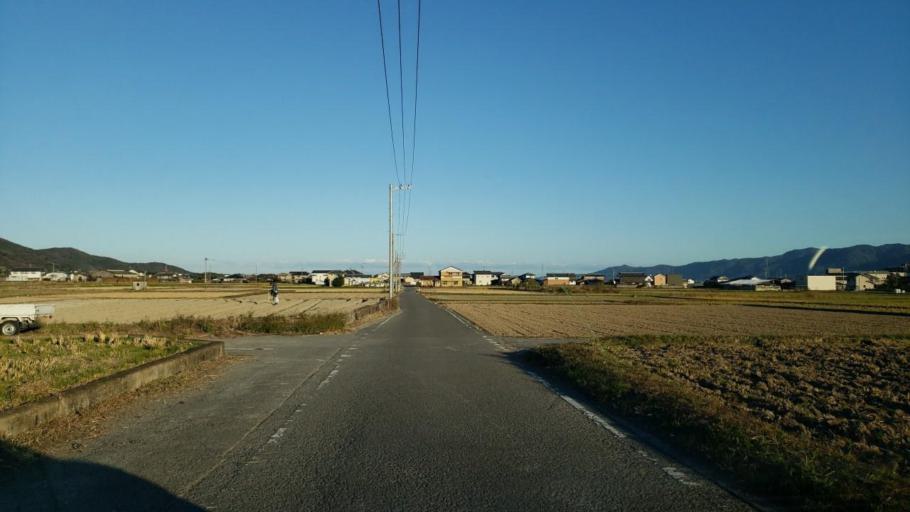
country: JP
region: Tokushima
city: Kamojimacho-jogejima
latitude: 34.0910
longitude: 134.2602
